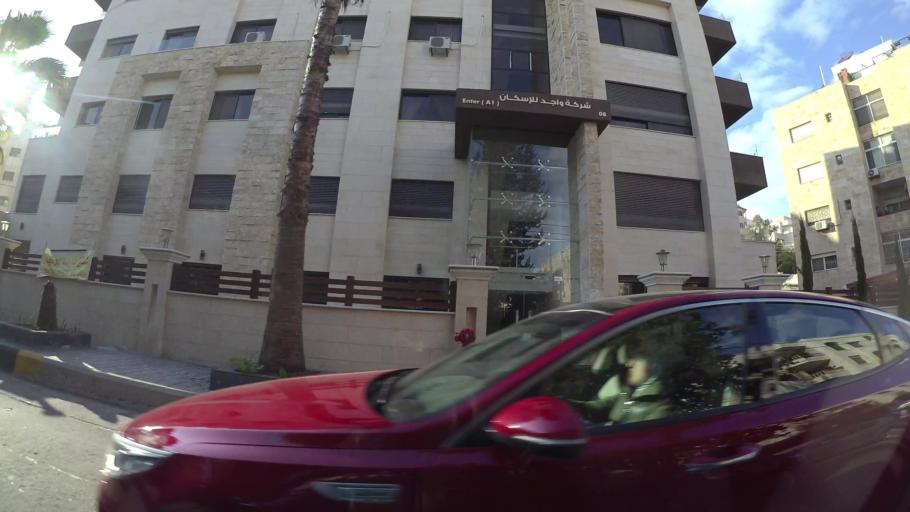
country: JO
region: Amman
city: Al Jubayhah
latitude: 31.9789
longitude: 35.8692
